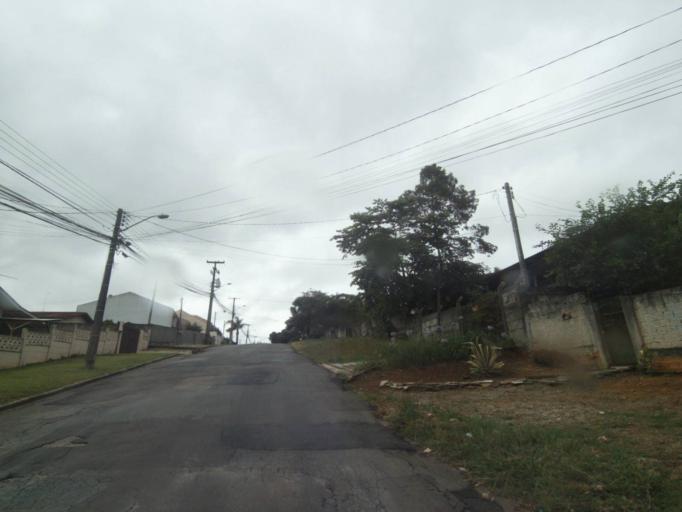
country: BR
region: Parana
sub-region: Curitiba
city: Curitiba
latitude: -25.4482
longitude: -49.3448
